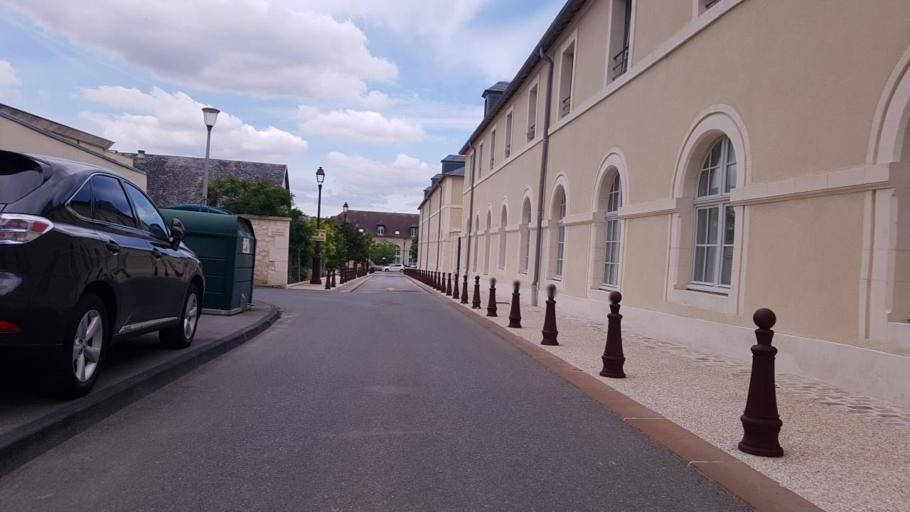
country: FR
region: Picardie
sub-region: Departement de l'Oise
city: Compiegne
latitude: 49.4210
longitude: 2.8309
